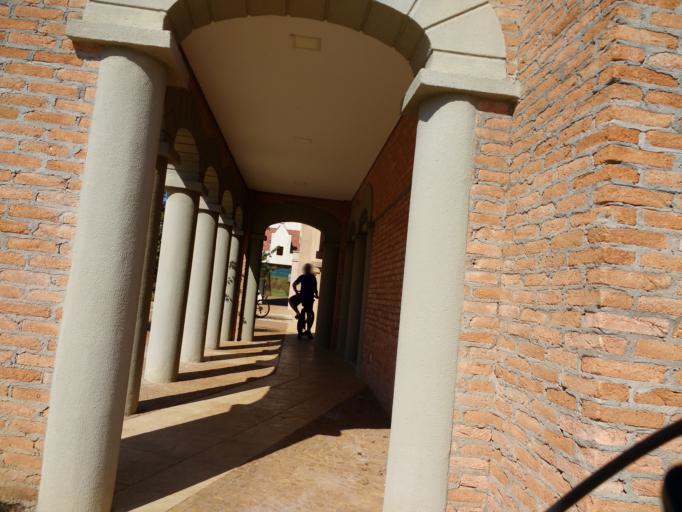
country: BR
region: Parana
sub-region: Londrina
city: Londrina
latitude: -23.3701
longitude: -51.1842
